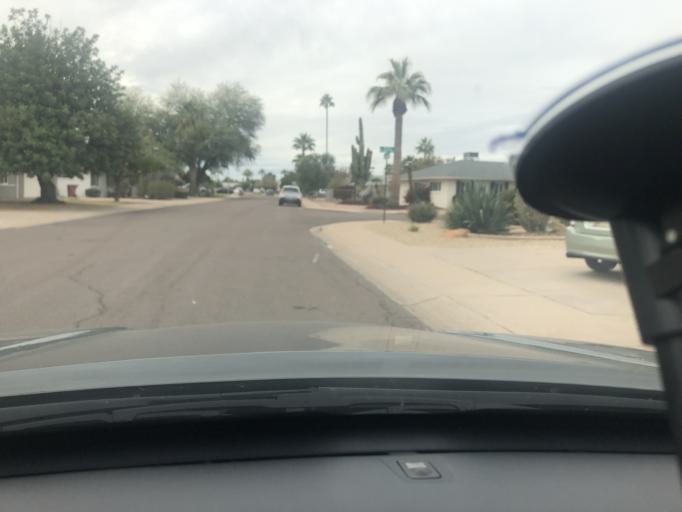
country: US
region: Arizona
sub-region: Maricopa County
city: Scottsdale
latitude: 33.4776
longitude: -111.9009
